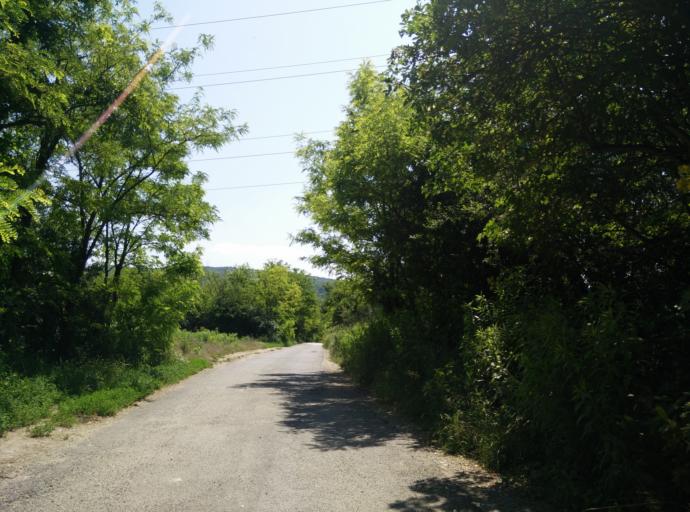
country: HU
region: Pest
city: Biatorbagy
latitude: 47.4595
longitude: 18.8214
